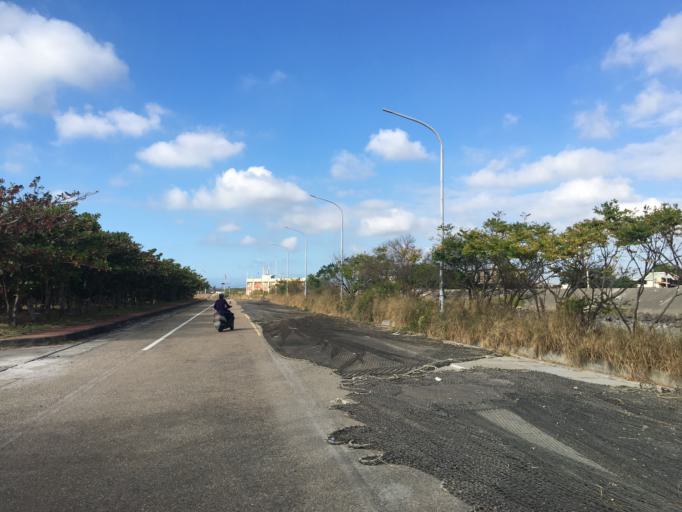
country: TW
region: Taiwan
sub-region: Hsinchu
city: Hsinchu
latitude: 24.7618
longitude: 120.9053
